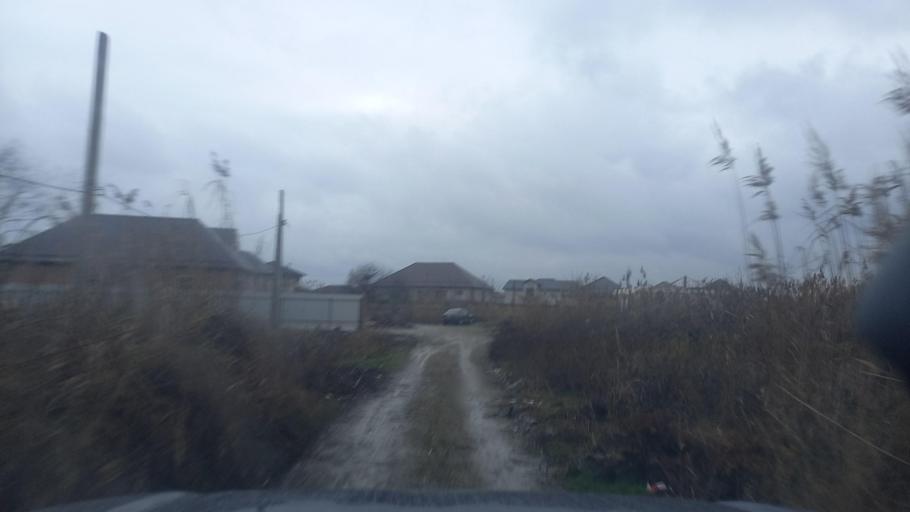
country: RU
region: Adygeya
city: Yablonovskiy
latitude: 44.9854
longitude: 38.9285
